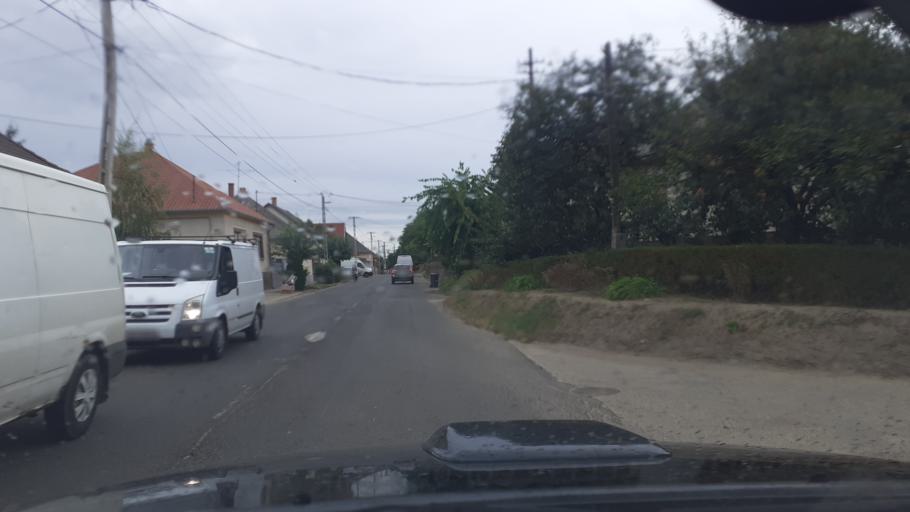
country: HU
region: Tolna
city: Dunafoldvar
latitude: 46.8014
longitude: 18.9305
